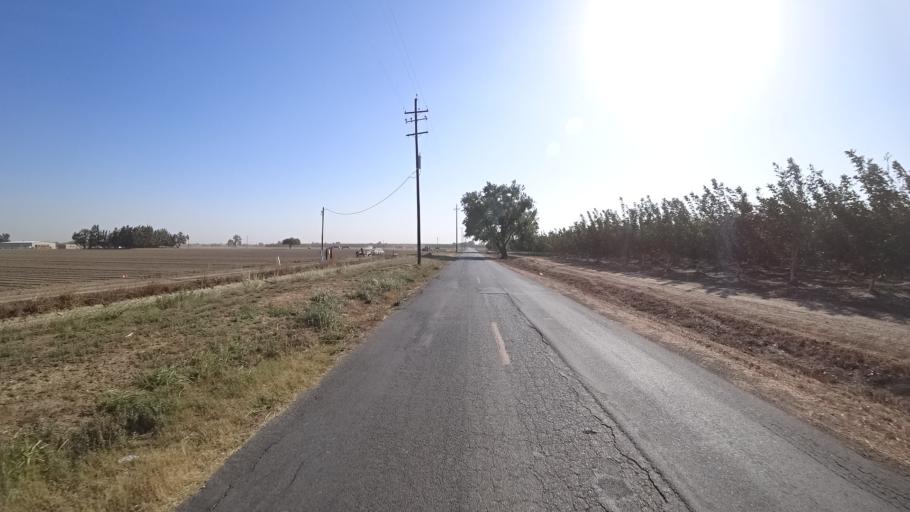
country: US
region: California
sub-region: Yolo County
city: Woodland
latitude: 38.7169
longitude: -121.8565
